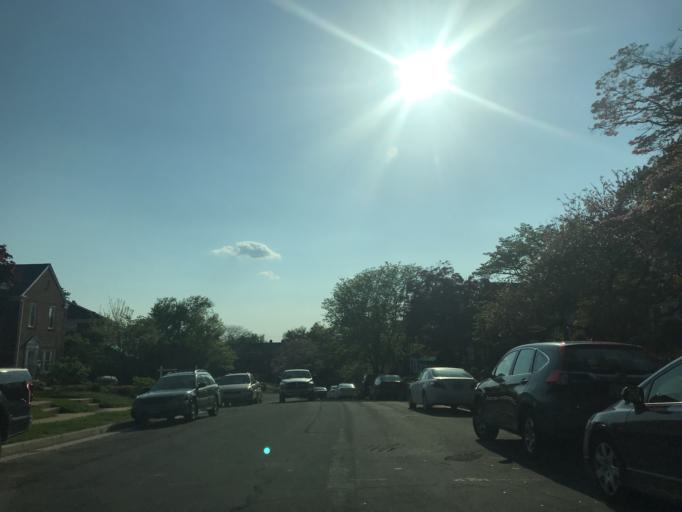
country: US
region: Maryland
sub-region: Baltimore County
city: Towson
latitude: 39.3839
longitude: -76.6159
